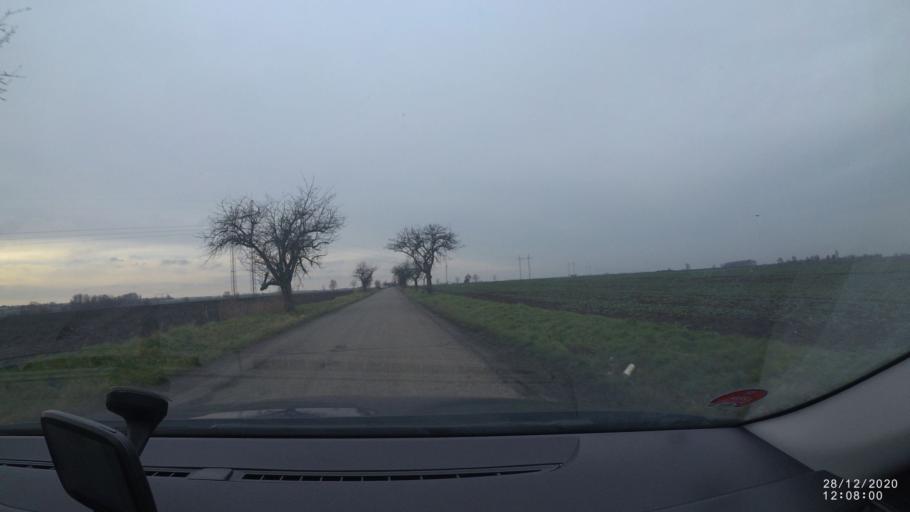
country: CZ
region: Central Bohemia
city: Zelenec
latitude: 50.1549
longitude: 14.6496
